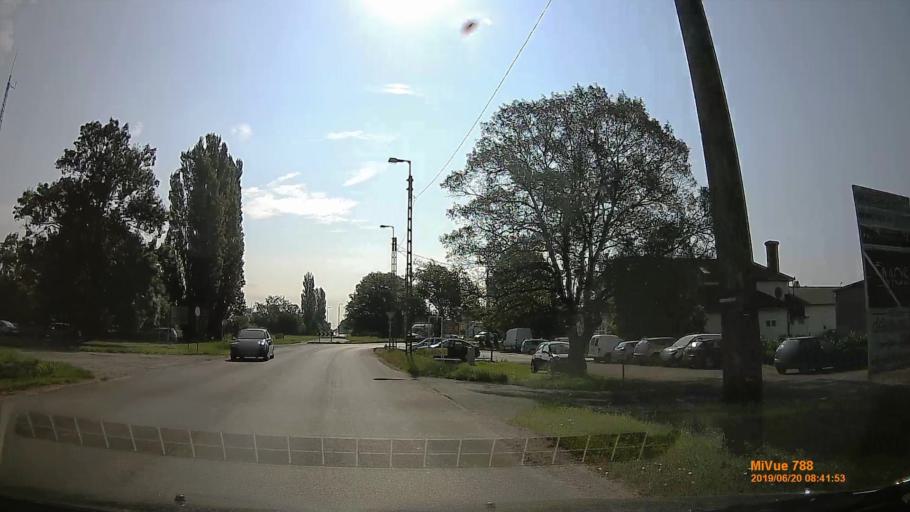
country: HU
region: Baranya
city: Szigetvar
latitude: 46.0485
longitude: 17.8181
